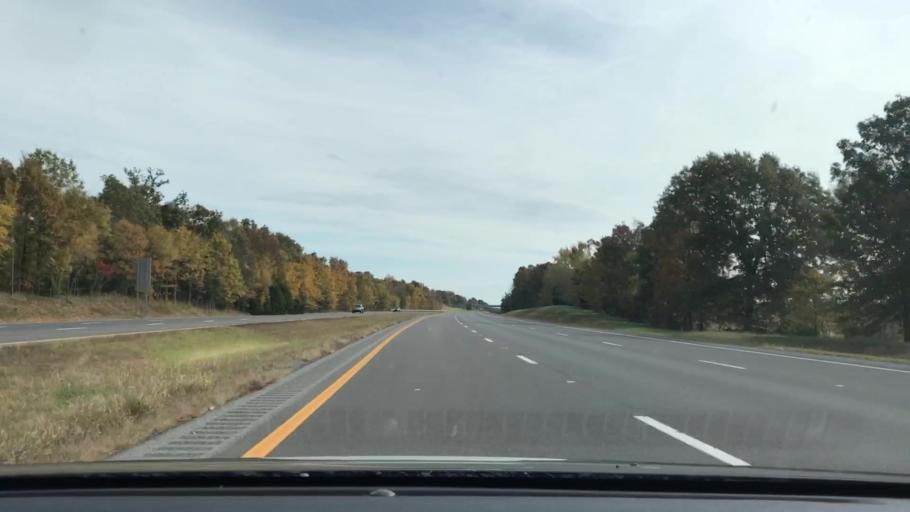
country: US
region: Kentucky
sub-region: Graves County
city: Mayfield
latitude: 36.7767
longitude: -88.5915
